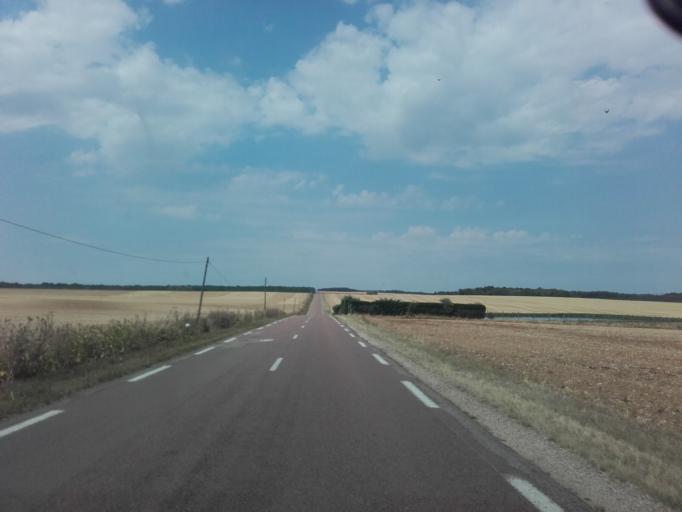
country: FR
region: Bourgogne
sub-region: Departement de l'Yonne
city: Joux-la-Ville
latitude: 47.6791
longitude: 3.8726
